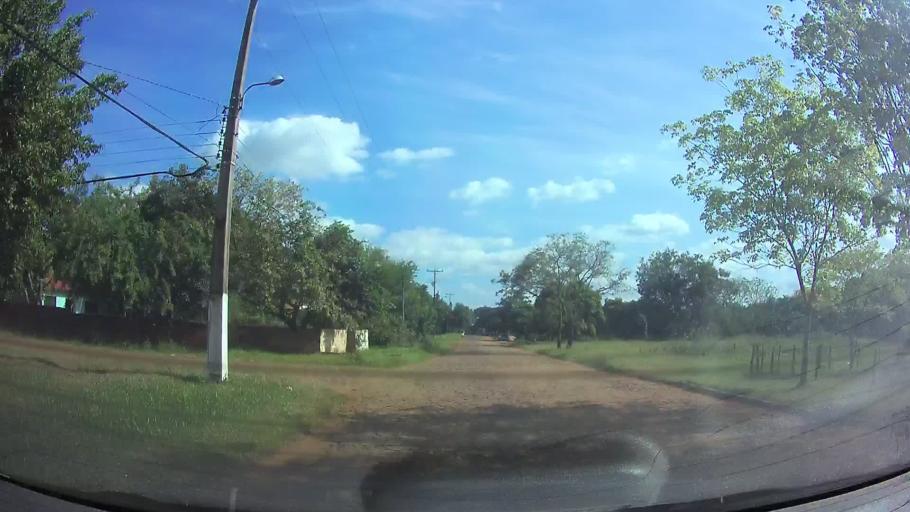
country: PY
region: Central
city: Limpio
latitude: -25.2490
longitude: -57.4701
